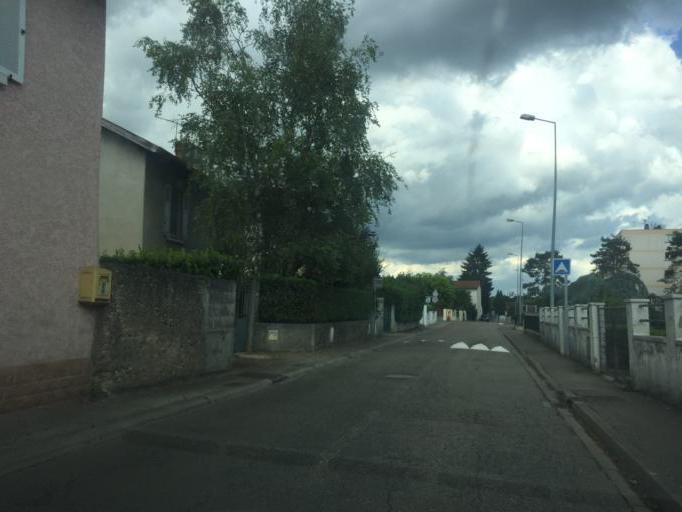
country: FR
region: Rhone-Alpes
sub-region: Departement de l'Isere
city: Pont-de-Cheruy
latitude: 45.7554
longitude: 5.1691
